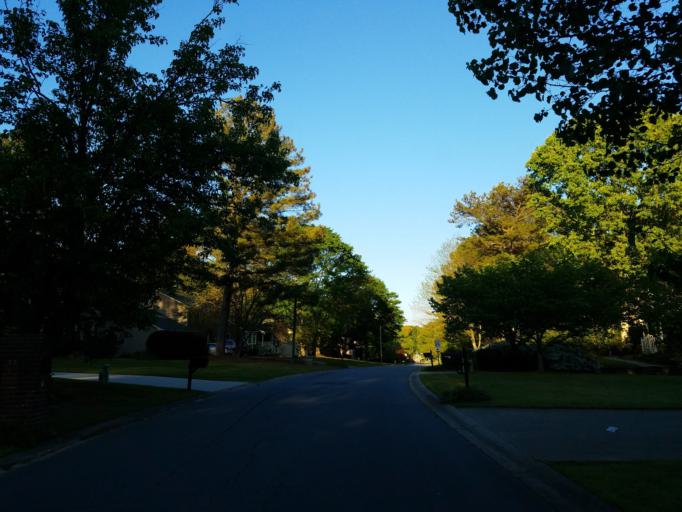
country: US
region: Georgia
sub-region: Cobb County
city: Powder Springs
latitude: 33.9198
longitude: -84.6346
